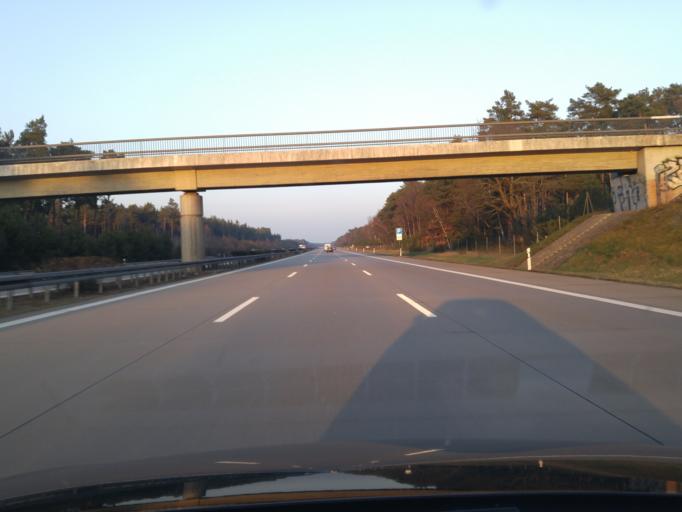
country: DE
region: Brandenburg
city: Wollin
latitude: 52.3154
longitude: 12.4881
